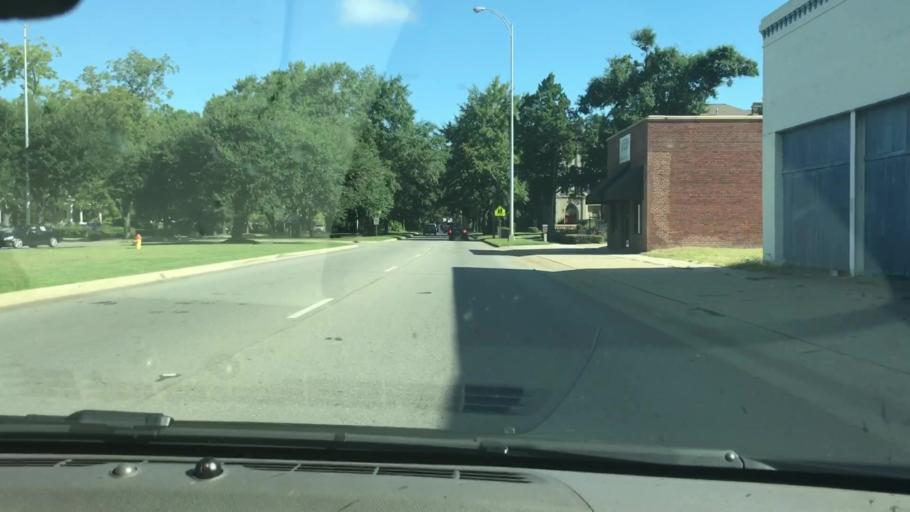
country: US
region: Alabama
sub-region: Barbour County
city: Eufaula
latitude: 31.8942
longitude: -85.1456
